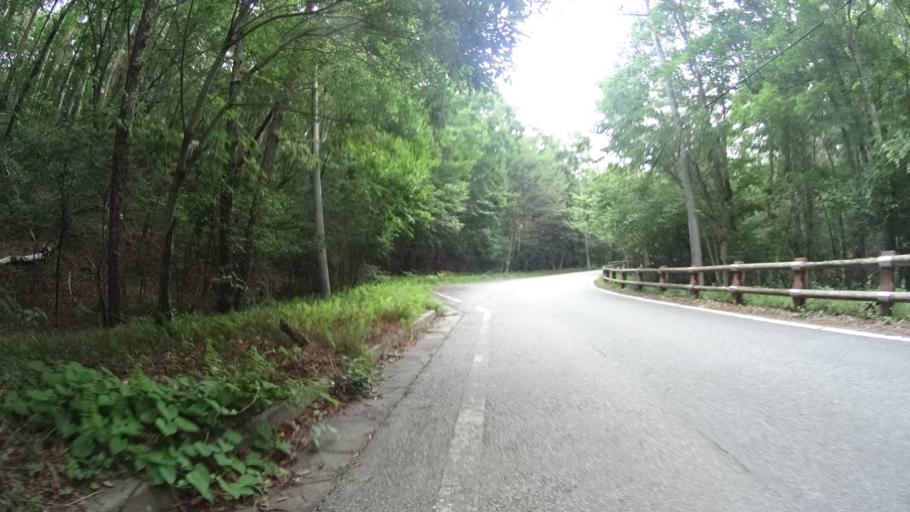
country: JP
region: Yamanashi
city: Nirasaki
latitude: 35.8911
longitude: 138.5666
